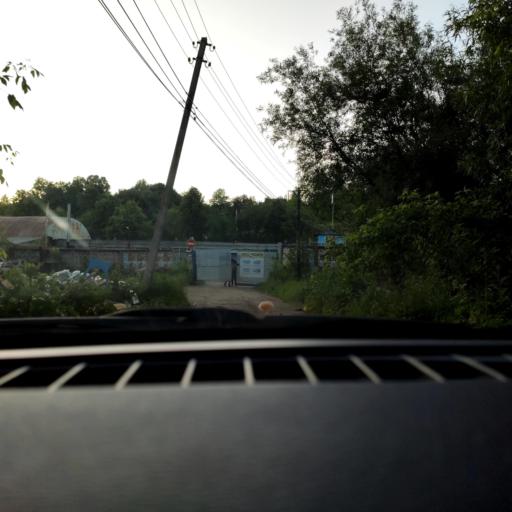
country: RU
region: Perm
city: Perm
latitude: 58.0728
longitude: 56.3556
